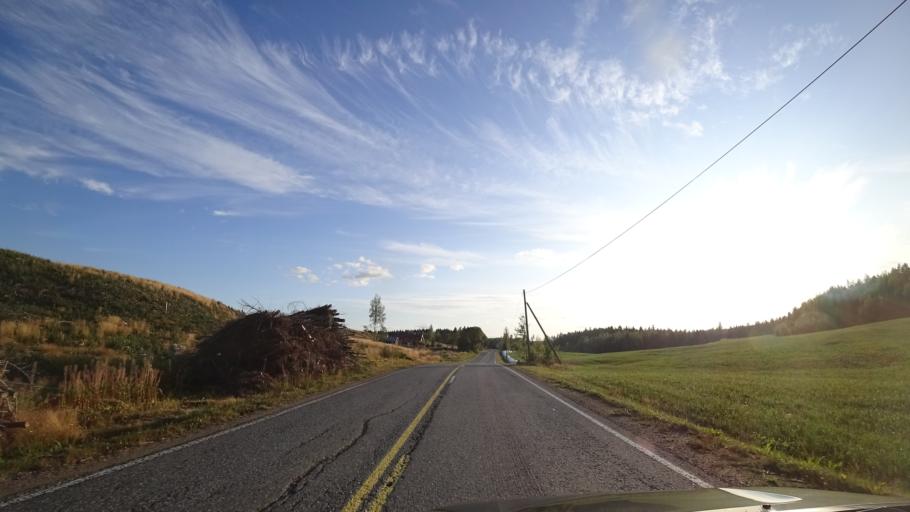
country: FI
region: Haeme
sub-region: Haemeenlinna
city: Lammi
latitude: 61.0514
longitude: 24.9562
